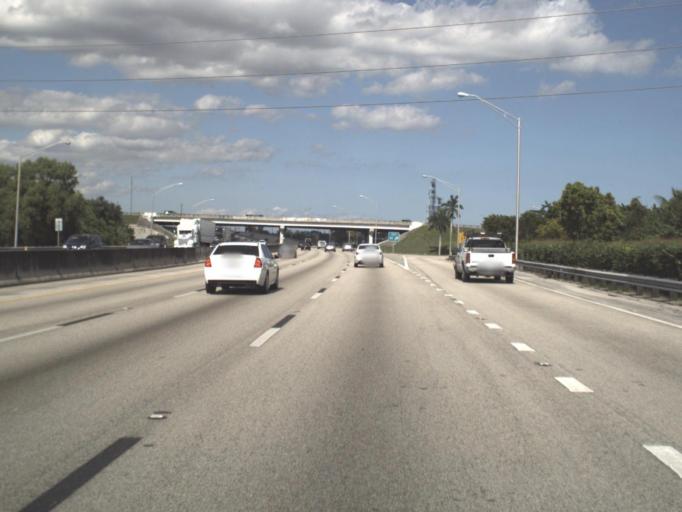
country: US
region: Florida
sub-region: Broward County
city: Pembroke Pines
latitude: 26.0035
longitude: -80.2161
